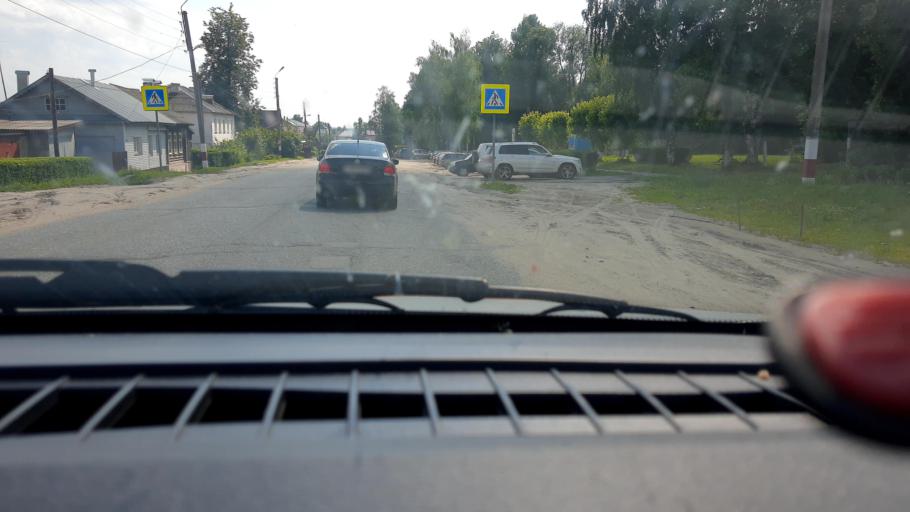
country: RU
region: Nizjnij Novgorod
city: Uren'
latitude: 57.4614
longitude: 45.7983
